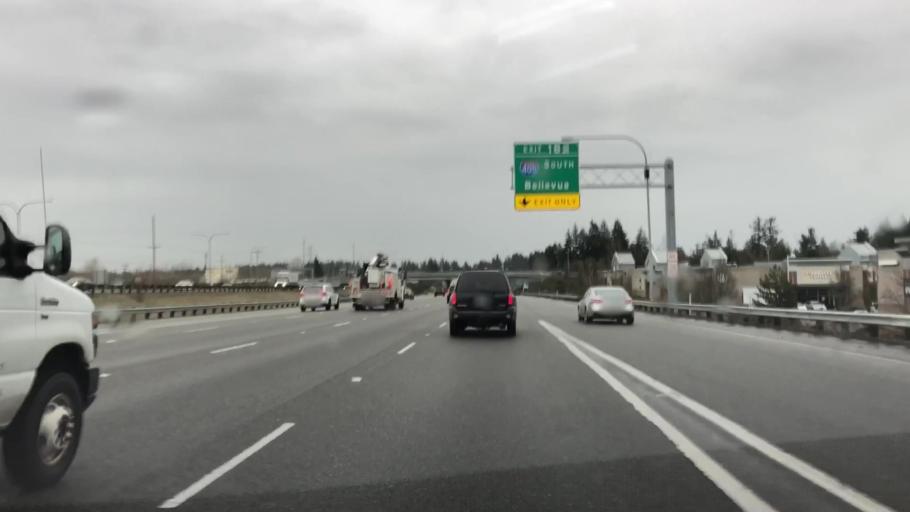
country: US
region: Washington
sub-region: Snohomish County
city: Alderwood Manor
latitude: 47.8232
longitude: -122.2733
